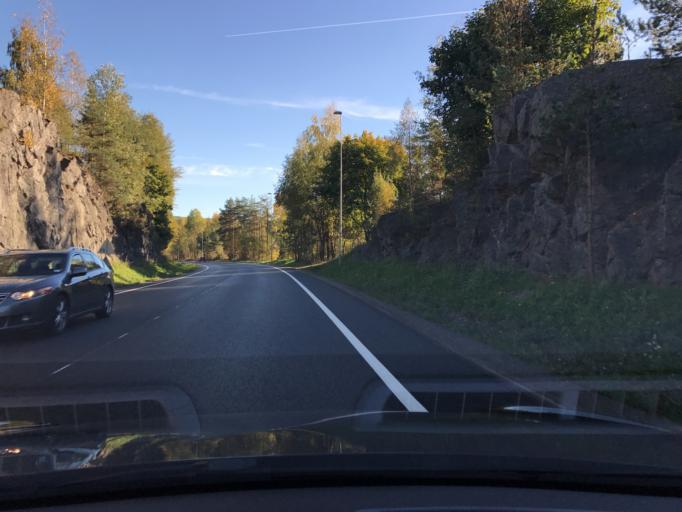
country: NO
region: Buskerud
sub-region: Nedre Eiker
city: Mjondalen
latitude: 59.7603
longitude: 9.9842
